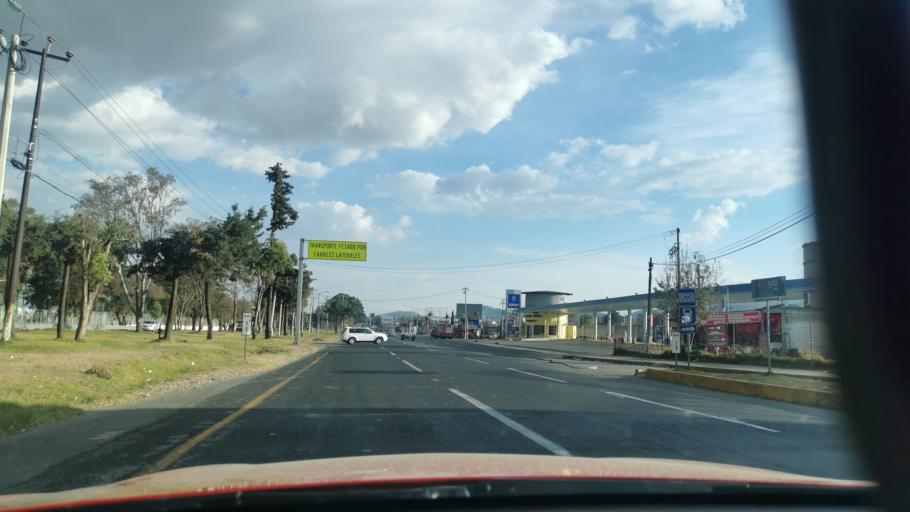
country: MX
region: Mexico
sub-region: Toluca
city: Barrio de Jesus Fraccion Primera
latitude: 19.3685
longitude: -99.6943
